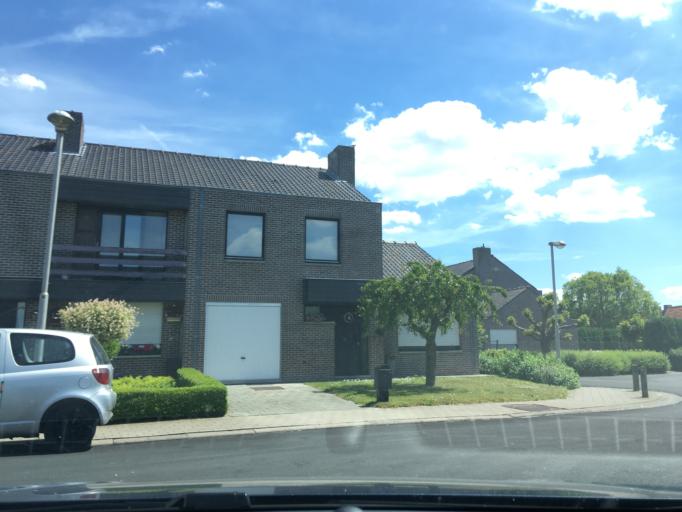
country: BE
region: Flanders
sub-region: Provincie West-Vlaanderen
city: Ardooie
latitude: 51.0024
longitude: 3.2071
